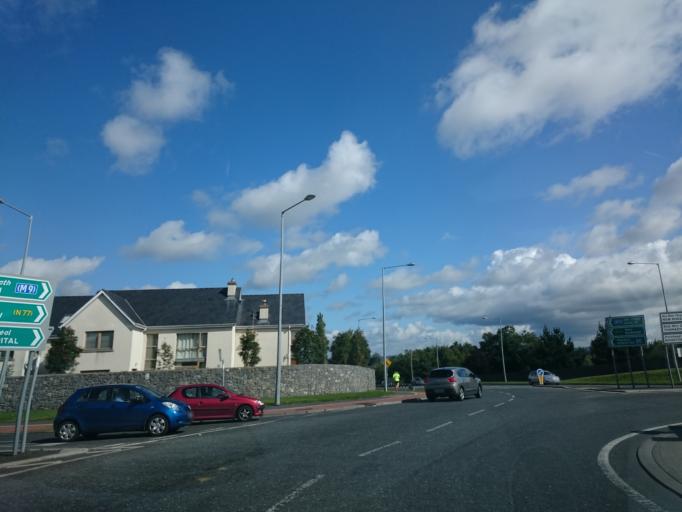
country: IE
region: Leinster
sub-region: Kilkenny
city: Kilkenny
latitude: 52.6419
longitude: -7.2315
